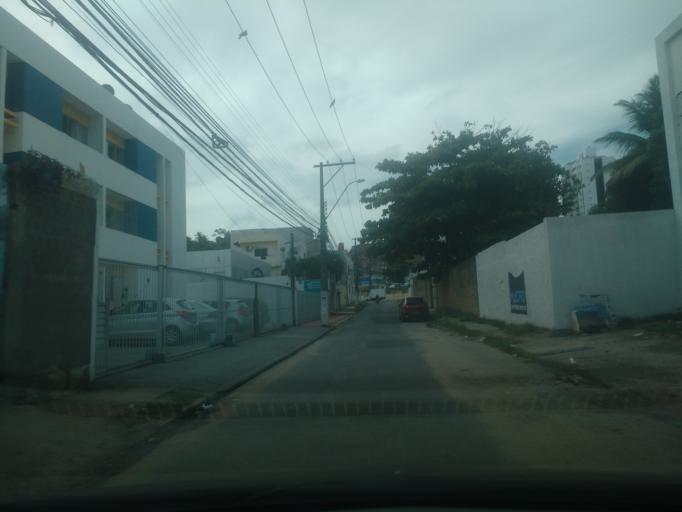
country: BR
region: Alagoas
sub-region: Maceio
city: Maceio
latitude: -9.6463
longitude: -35.7128
